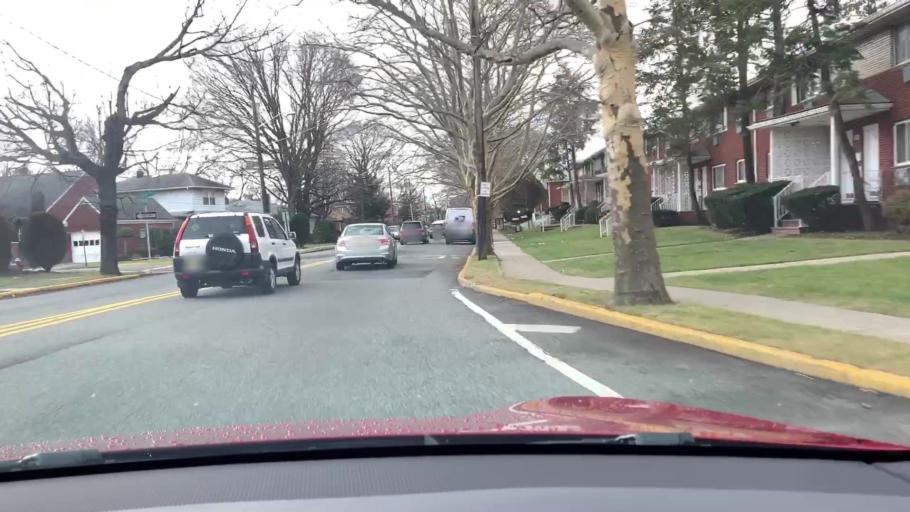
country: US
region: New Jersey
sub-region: Bergen County
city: Fort Lee
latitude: 40.8447
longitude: -73.9788
